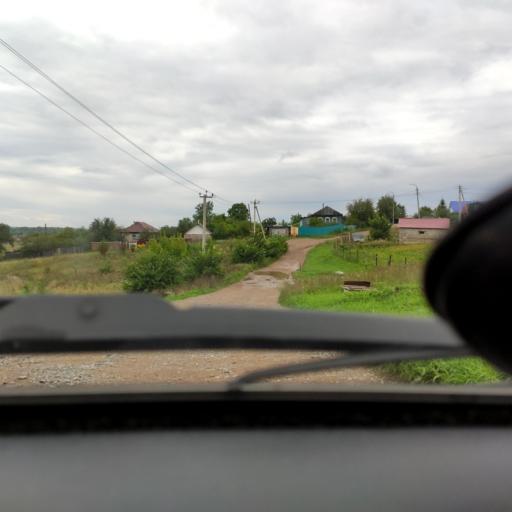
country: RU
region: Bashkortostan
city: Blagoveshchensk
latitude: 54.8928
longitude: 56.0398
